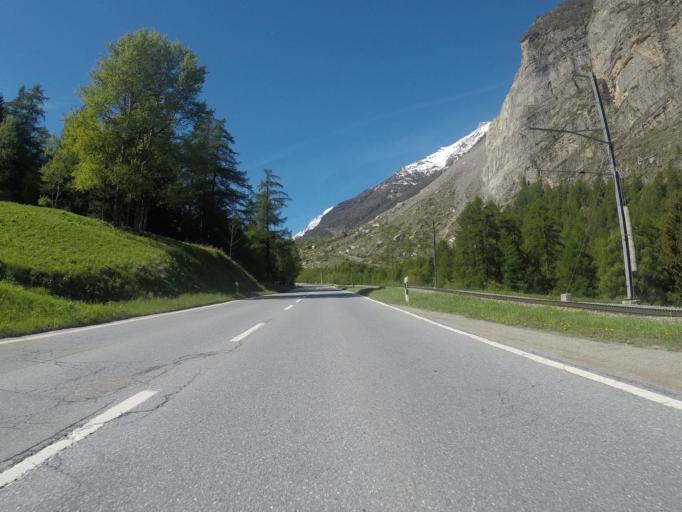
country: CH
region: Valais
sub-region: Visp District
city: Sankt Niklaus
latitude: 46.1188
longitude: 7.7876
